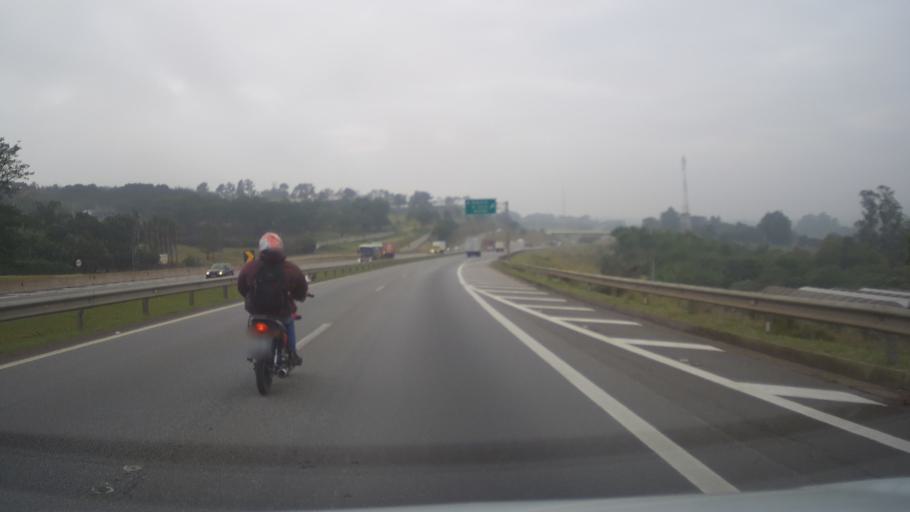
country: BR
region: Sao Paulo
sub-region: Jarinu
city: Jarinu
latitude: -23.0659
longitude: -46.6457
